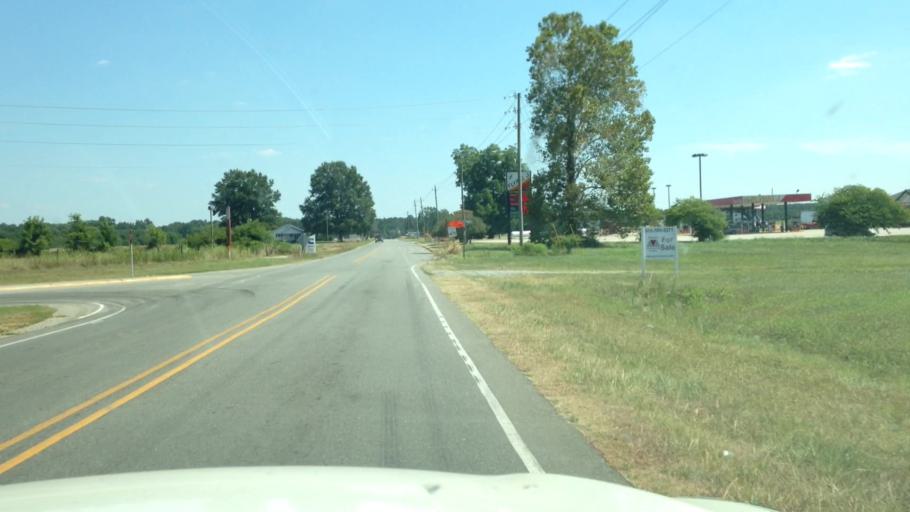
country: US
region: North Carolina
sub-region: Johnston County
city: Kenly
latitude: 35.5764
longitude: -78.1458
